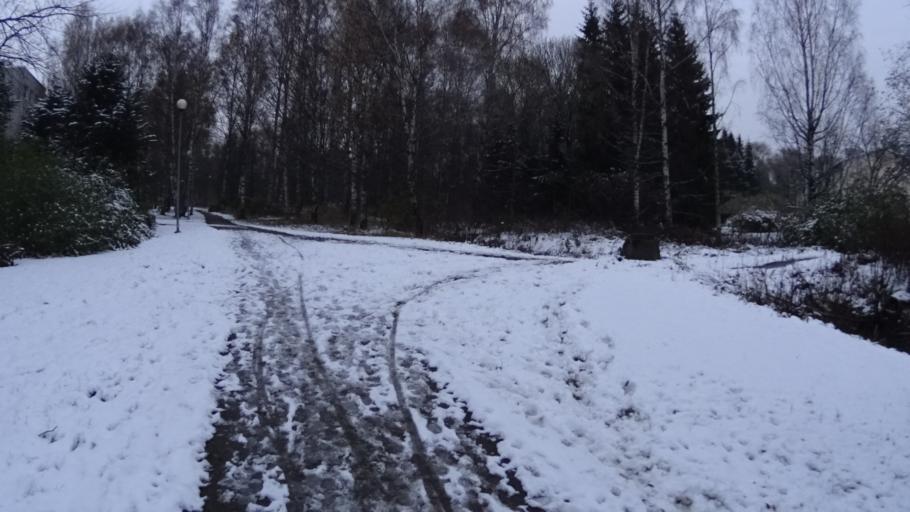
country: FI
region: Uusimaa
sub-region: Helsinki
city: Otaniemi
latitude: 60.1836
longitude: 24.8085
